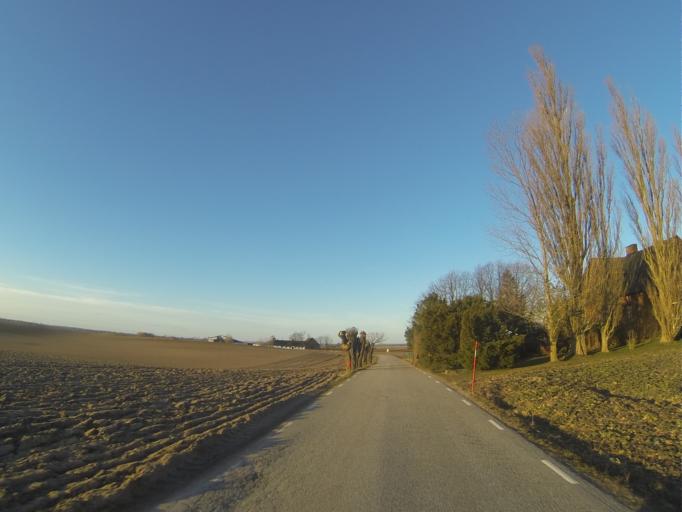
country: SE
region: Skane
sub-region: Staffanstorps Kommun
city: Staffanstorp
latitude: 55.5979
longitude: 13.1803
